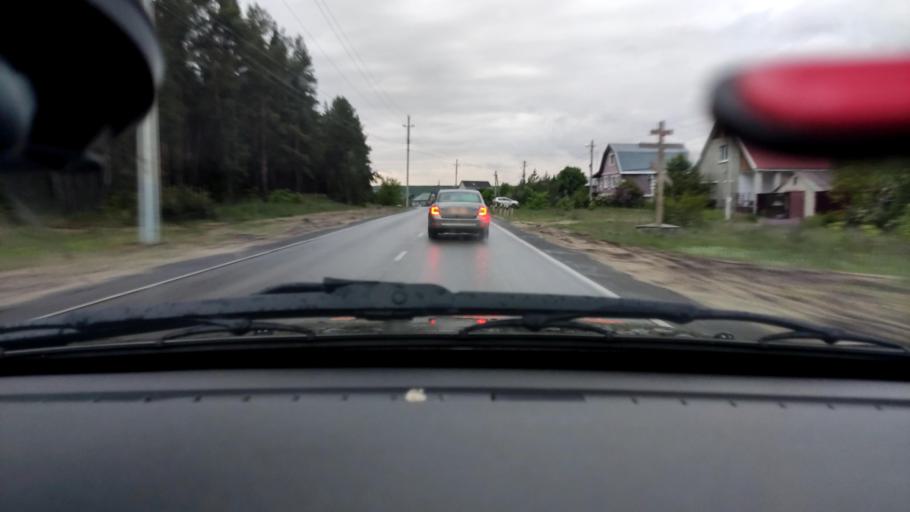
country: RU
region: Voronezj
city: Shilovo
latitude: 51.5988
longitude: 39.0322
